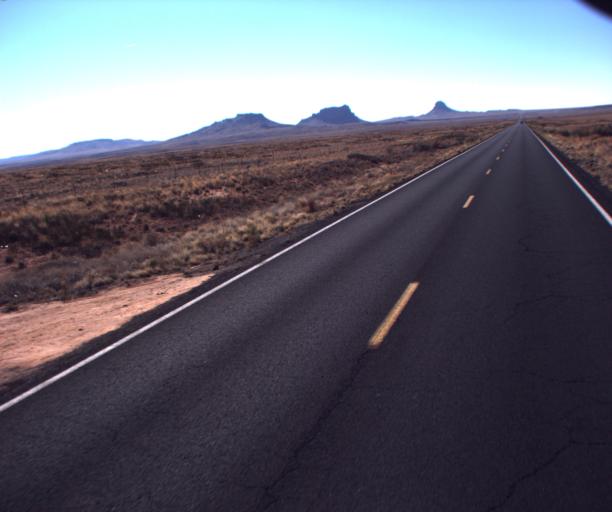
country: US
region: Arizona
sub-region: Navajo County
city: Dilkon
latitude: 35.3837
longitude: -110.4255
